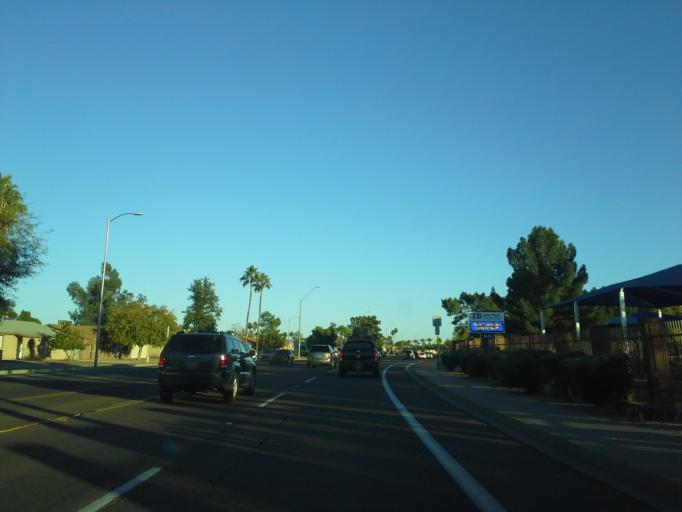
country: US
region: Arizona
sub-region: Maricopa County
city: Paradise Valley
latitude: 33.6132
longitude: -112.0035
